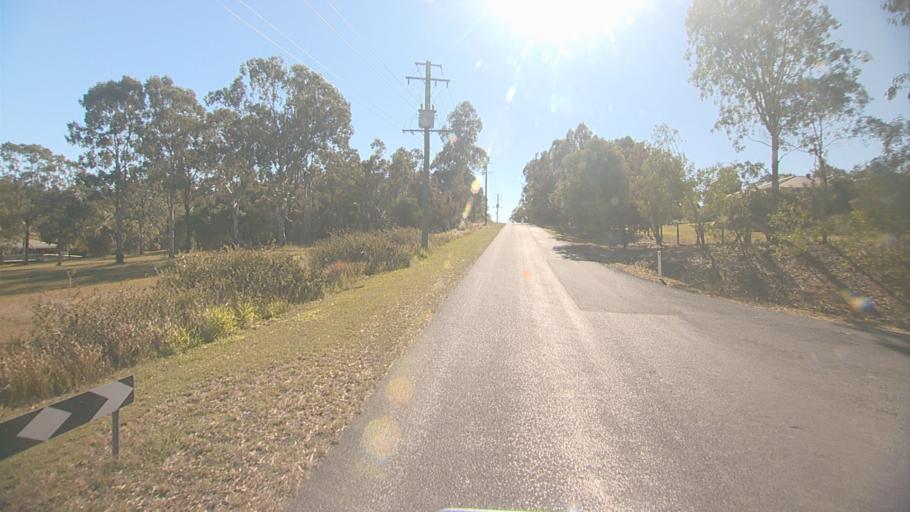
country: AU
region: Queensland
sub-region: Logan
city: Chambers Flat
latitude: -27.7797
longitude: 153.1409
